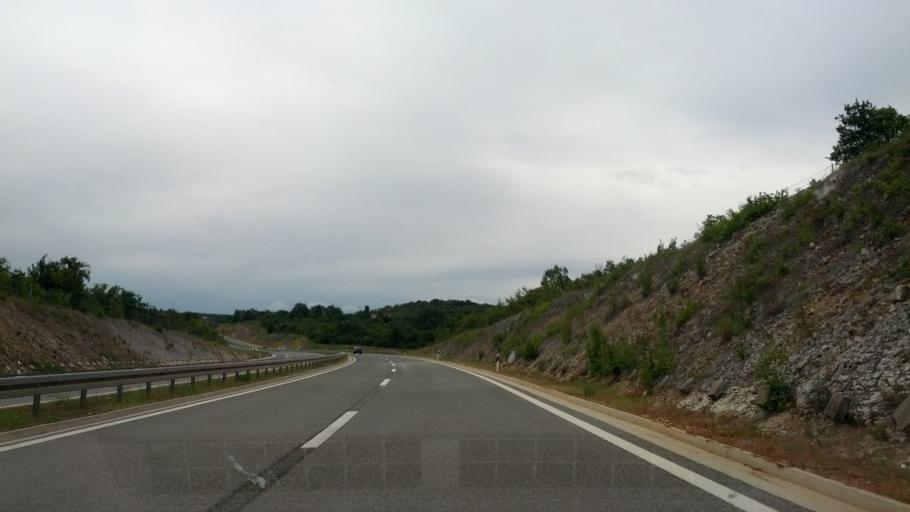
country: HR
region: Istarska
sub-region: Grad Rovinj
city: Rovinj
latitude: 45.1563
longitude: 13.7314
